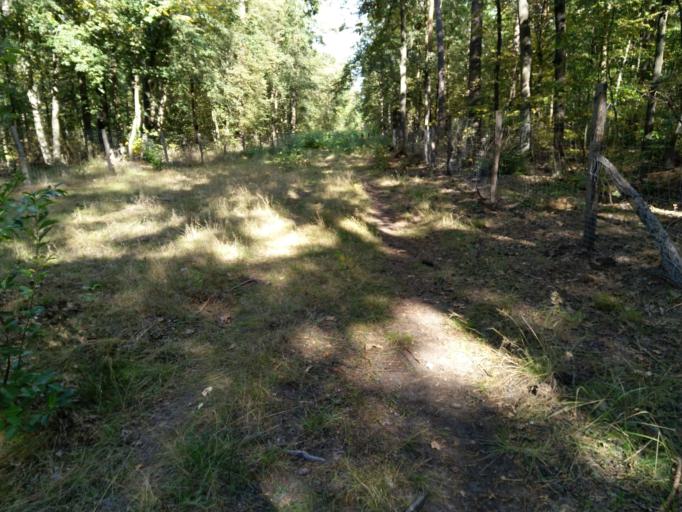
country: DE
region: Brandenburg
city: Erkner
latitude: 52.4367
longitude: 13.7269
